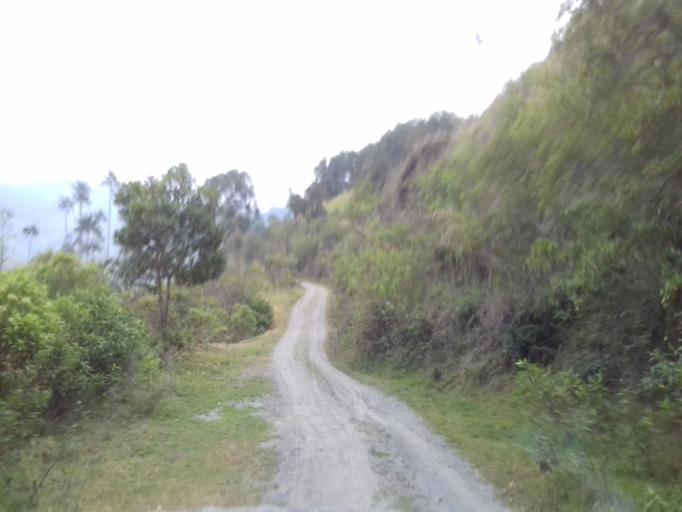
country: CO
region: Tolima
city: Cajamarca
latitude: 4.5342
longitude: -75.4604
